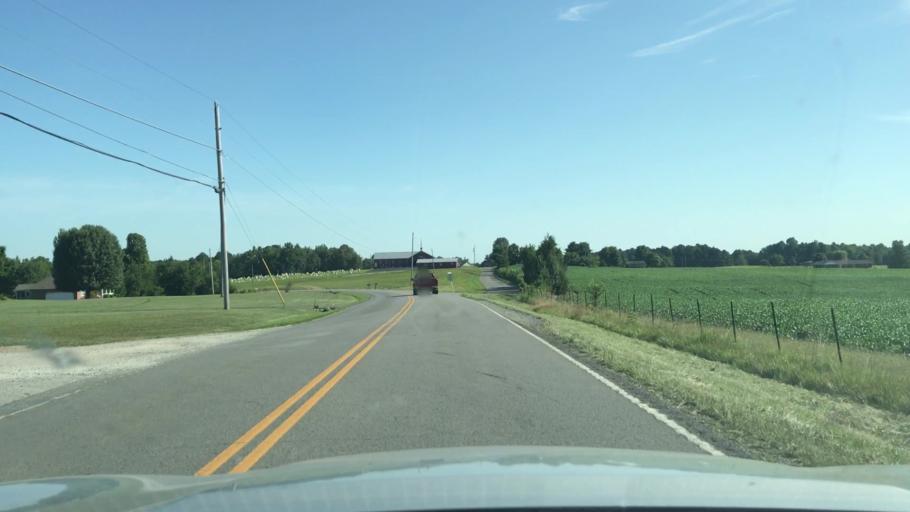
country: US
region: Kentucky
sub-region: Muhlenberg County
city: Greenville
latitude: 37.1765
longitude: -87.1526
